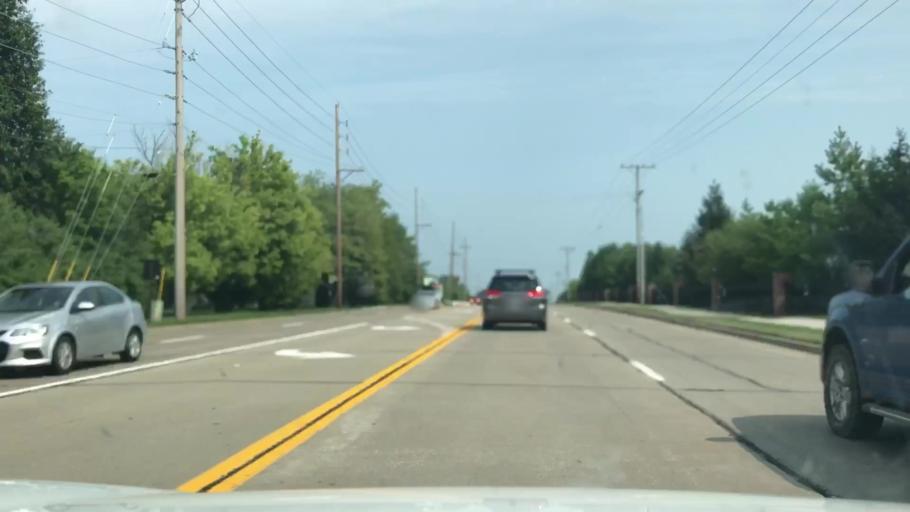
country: US
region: Missouri
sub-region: Saint Charles County
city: Dardenne Prairie
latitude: 38.7785
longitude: -90.7374
